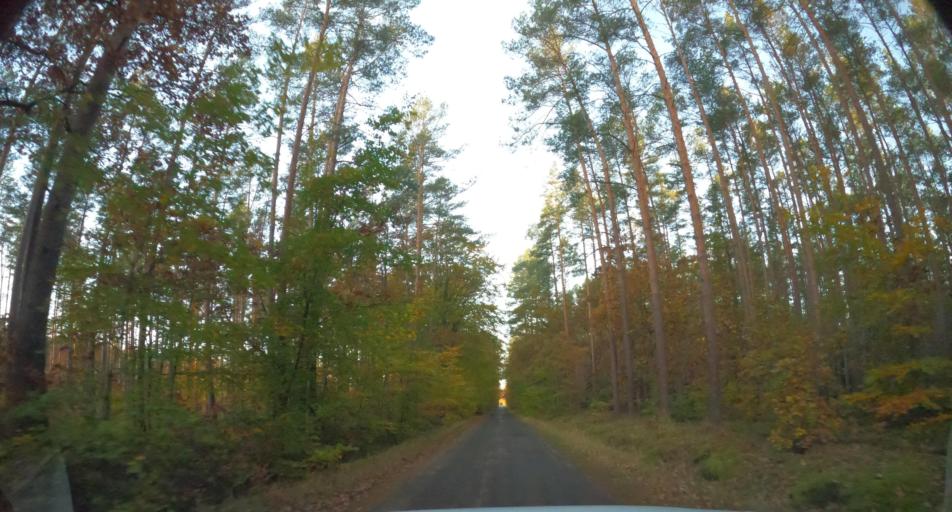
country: PL
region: West Pomeranian Voivodeship
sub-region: Powiat policki
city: Nowe Warpno
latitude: 53.6450
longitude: 14.3242
